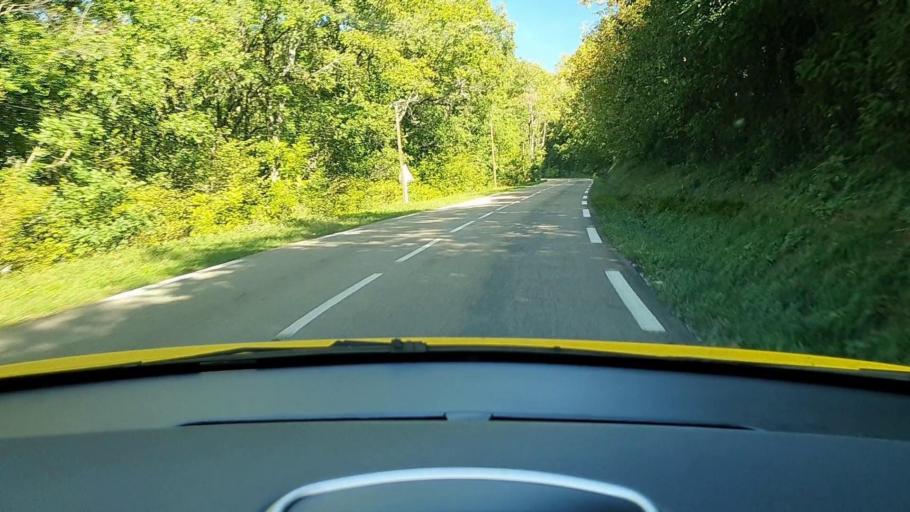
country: FR
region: Languedoc-Roussillon
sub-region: Departement du Gard
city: Le Vigan
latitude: 43.9678
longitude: 3.4176
